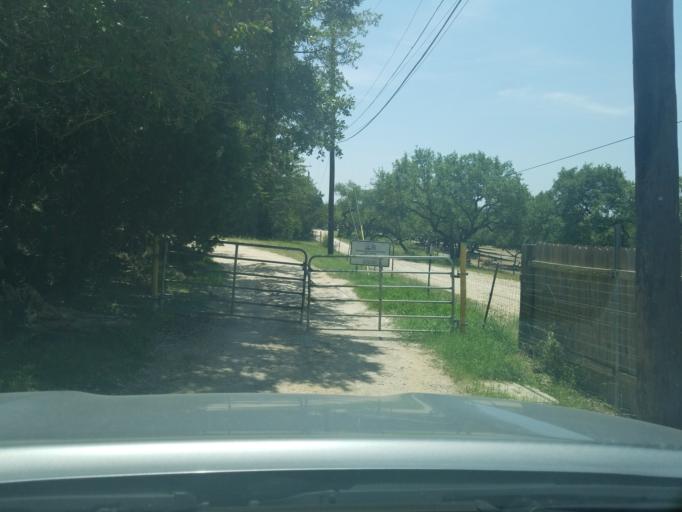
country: US
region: Texas
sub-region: Bexar County
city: Timberwood Park
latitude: 29.6837
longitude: -98.4932
